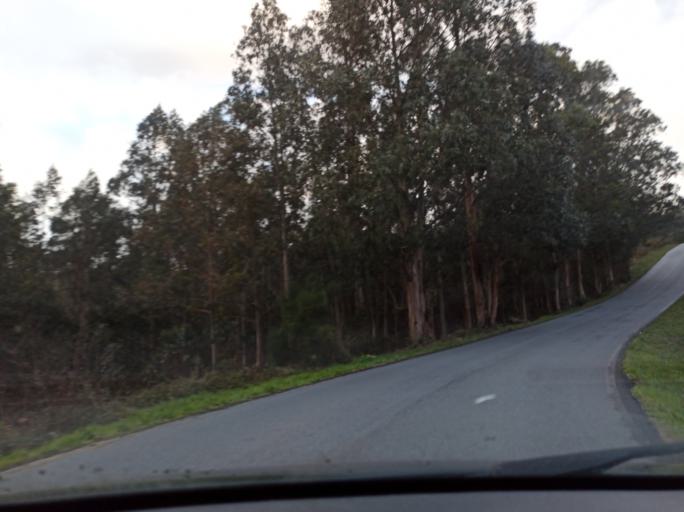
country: ES
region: Galicia
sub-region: Provincia da Coruna
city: Culleredo
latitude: 43.3016
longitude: -8.4329
